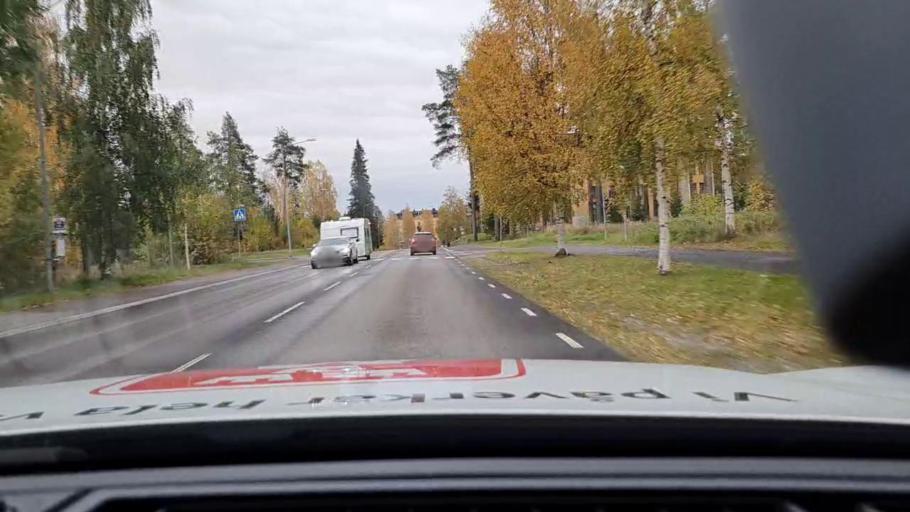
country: SE
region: Norrbotten
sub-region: Bodens Kommun
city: Boden
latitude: 65.8154
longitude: 21.6736
